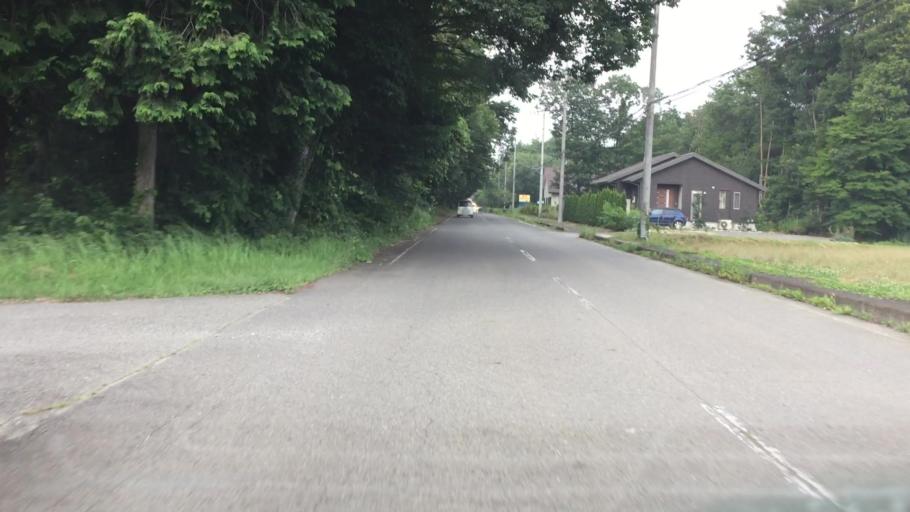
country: JP
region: Tochigi
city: Kuroiso
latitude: 36.9336
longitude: 139.9577
